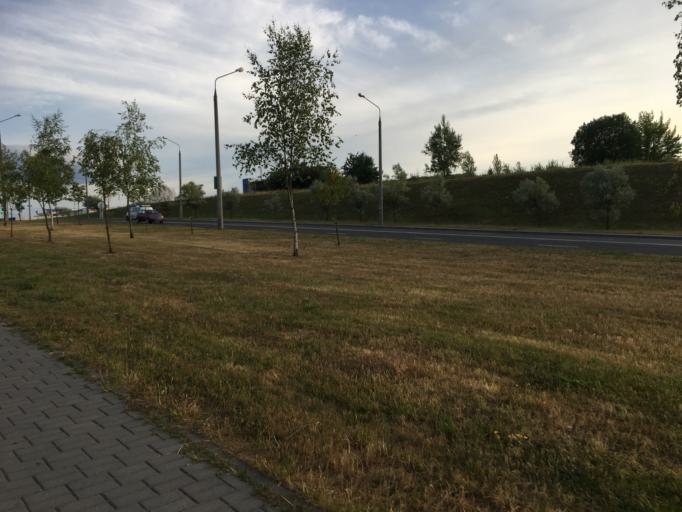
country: BY
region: Grodnenskaya
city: Hrodna
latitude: 53.7182
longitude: 23.8403
